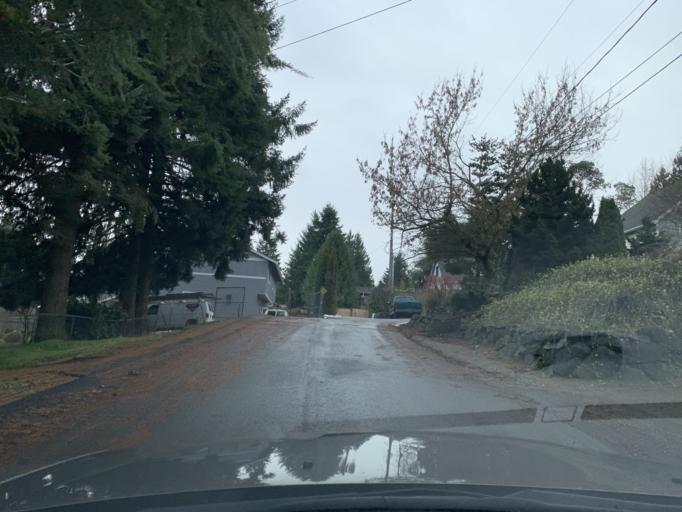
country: US
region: Washington
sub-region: King County
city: Tukwila
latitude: 47.4608
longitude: -122.2752
